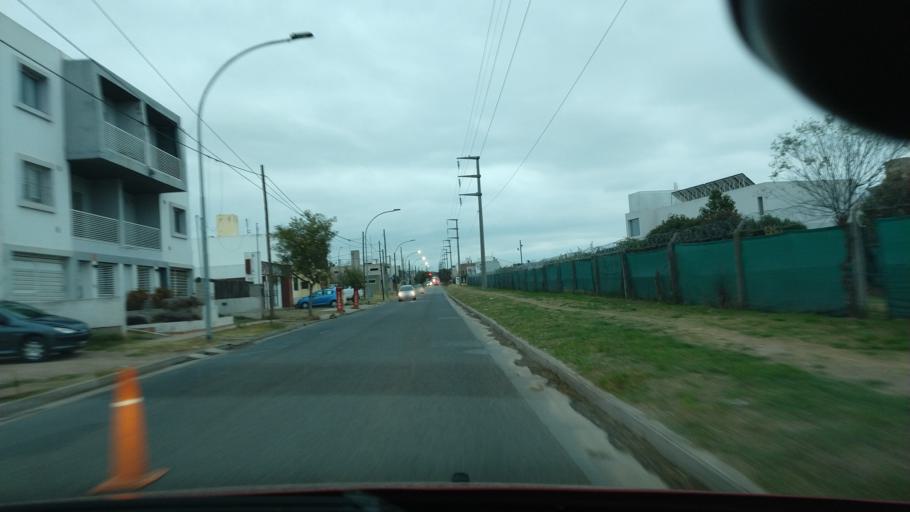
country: AR
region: Cordoba
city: La Calera
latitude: -31.3785
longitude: -64.2662
